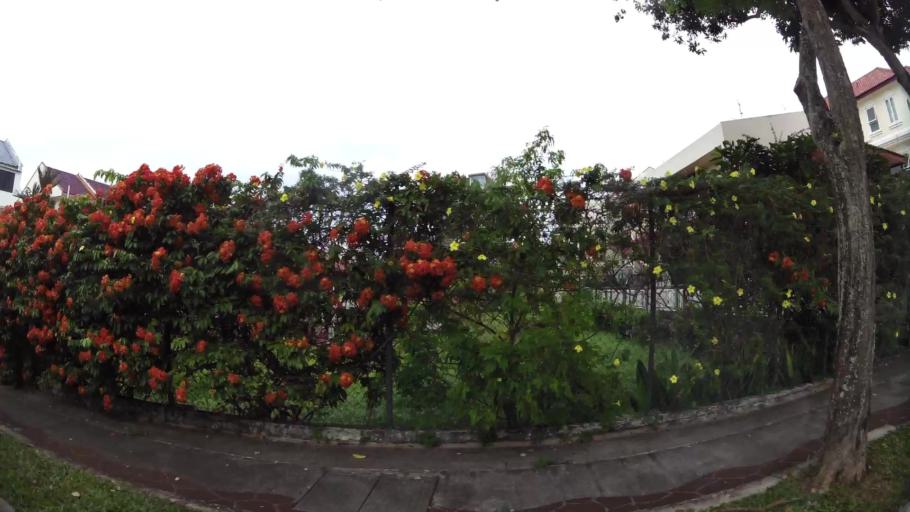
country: SG
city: Singapore
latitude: 1.3594
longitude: 103.8759
